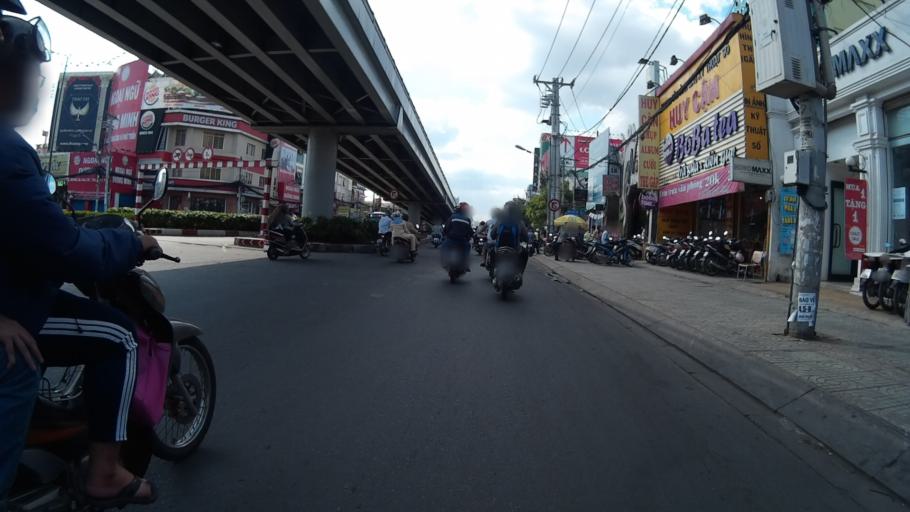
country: VN
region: Ho Chi Minh City
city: Quan Phu Nhuan
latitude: 10.8008
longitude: 106.6612
